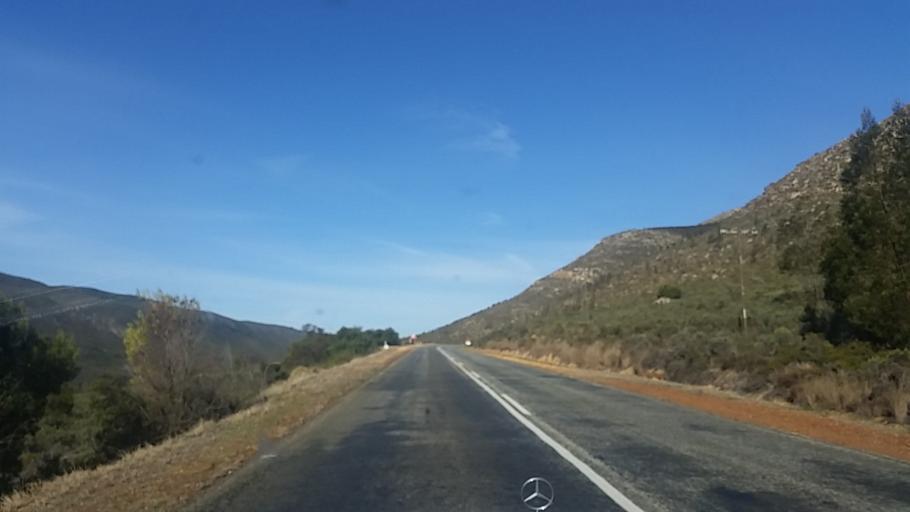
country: ZA
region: Western Cape
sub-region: Eden District Municipality
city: Knysna
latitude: -33.7485
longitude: 22.9744
